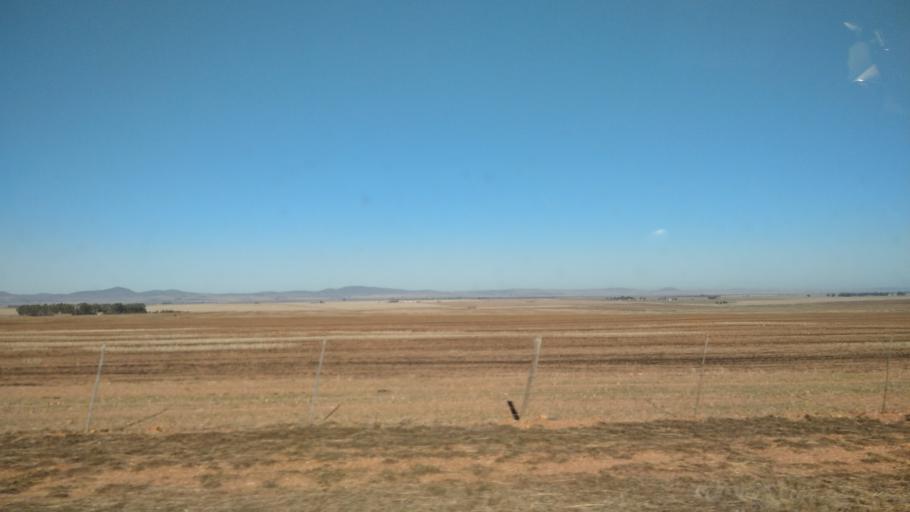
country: ZA
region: Western Cape
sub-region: West Coast District Municipality
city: Moorreesburg
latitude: -33.3214
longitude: 18.6262
